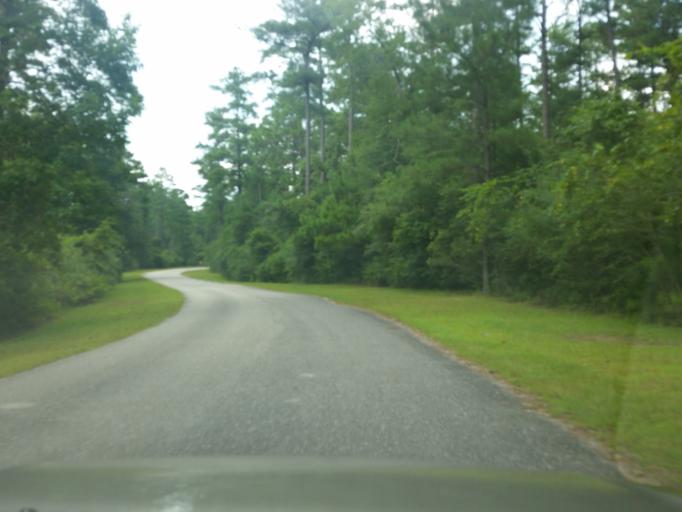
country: US
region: Alabama
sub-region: Baldwin County
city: Spanish Fort
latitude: 30.7393
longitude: -87.9092
